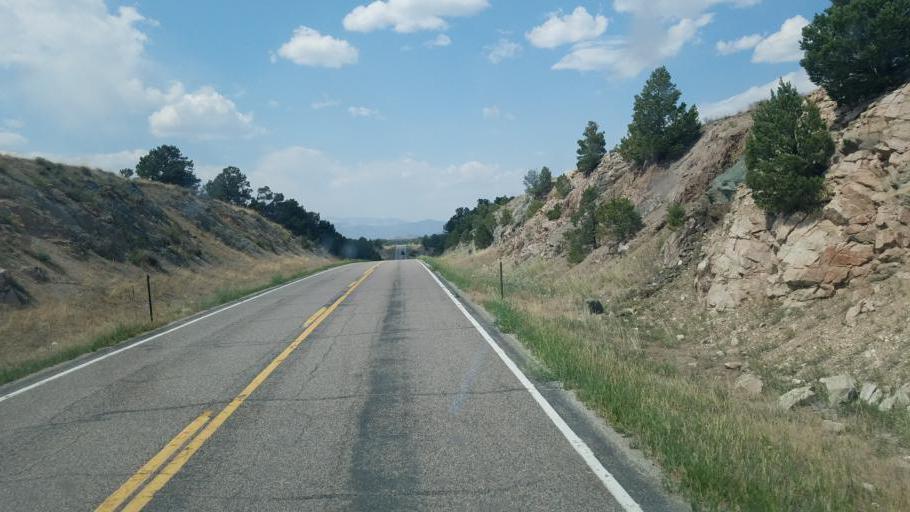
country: US
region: Colorado
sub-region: Custer County
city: Westcliffe
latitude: 38.2997
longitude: -105.6206
